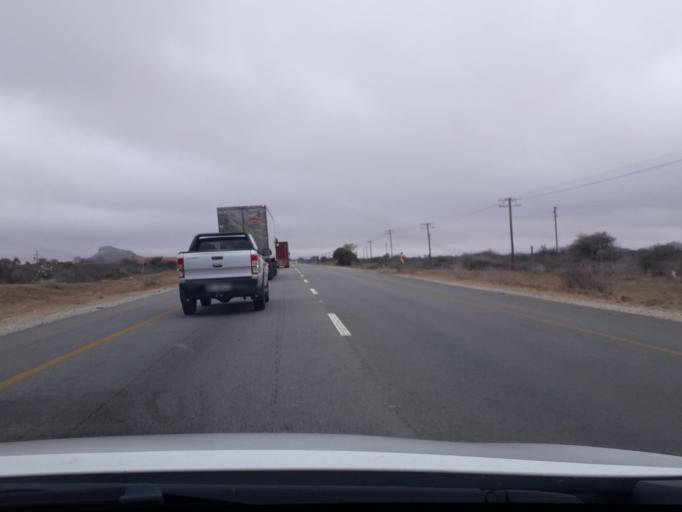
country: ZA
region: Limpopo
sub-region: Capricorn District Municipality
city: Mankoeng
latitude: -23.5244
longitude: 29.7070
